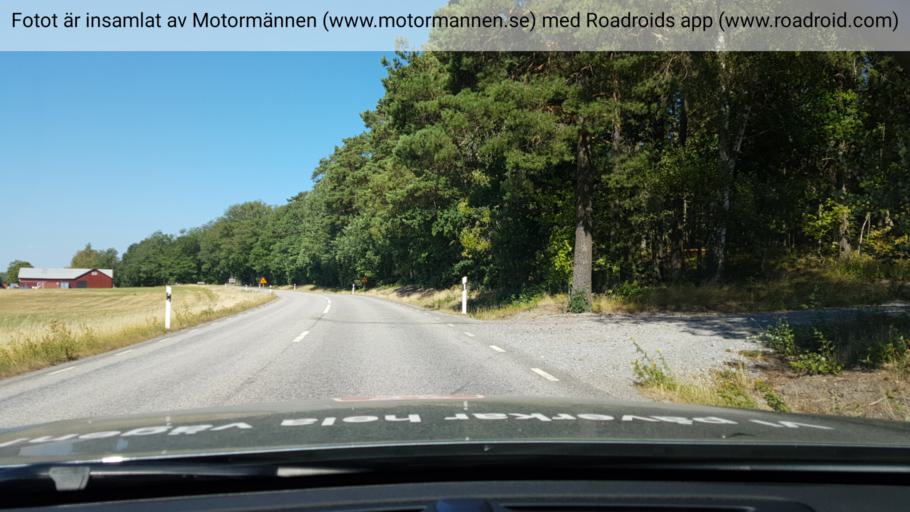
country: SE
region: Stockholm
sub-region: Ekero Kommun
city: Ekeroe
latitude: 59.2834
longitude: 17.7373
